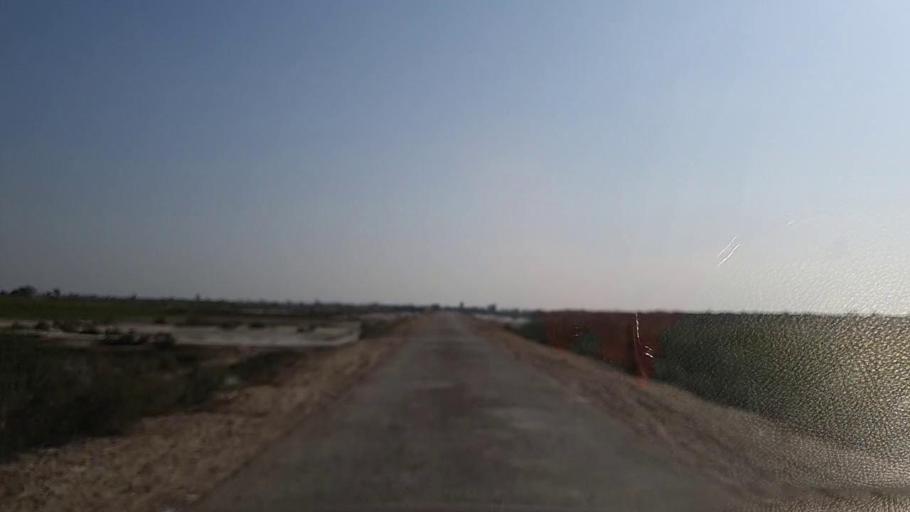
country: PK
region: Sindh
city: Sanghar
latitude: 26.0028
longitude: 69.0230
